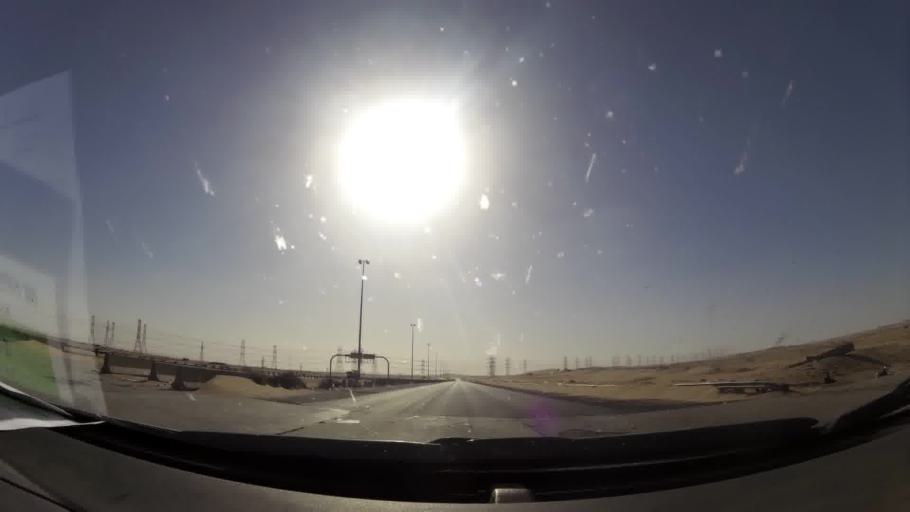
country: KW
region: Al Asimah
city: Kuwait City
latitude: 29.6327
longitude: 47.9310
